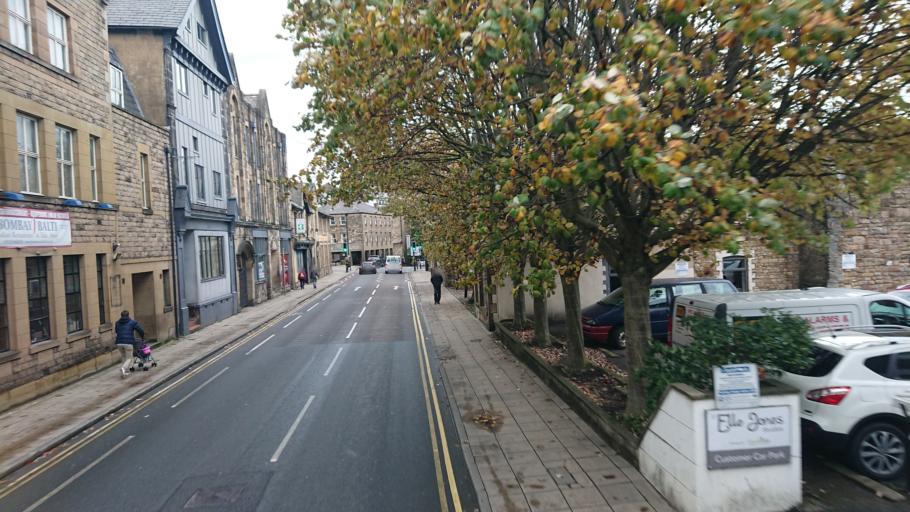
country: GB
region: England
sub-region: Lancashire
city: Lancaster
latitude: 54.0494
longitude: -2.8032
